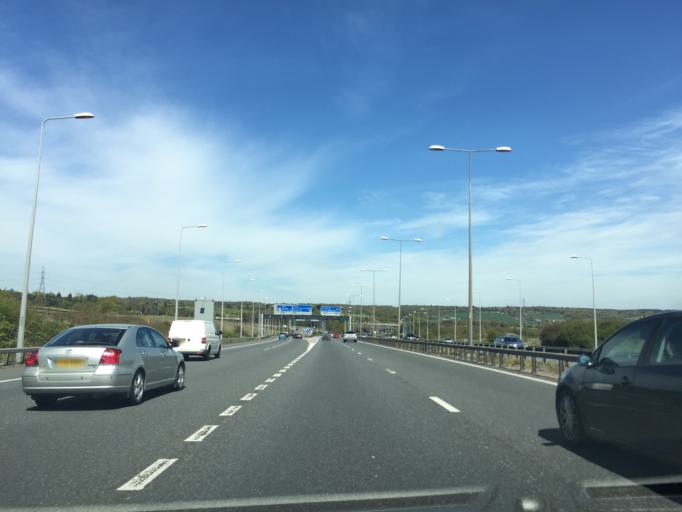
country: GB
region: England
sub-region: Essex
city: Theydon Bois
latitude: 51.6728
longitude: 0.1196
